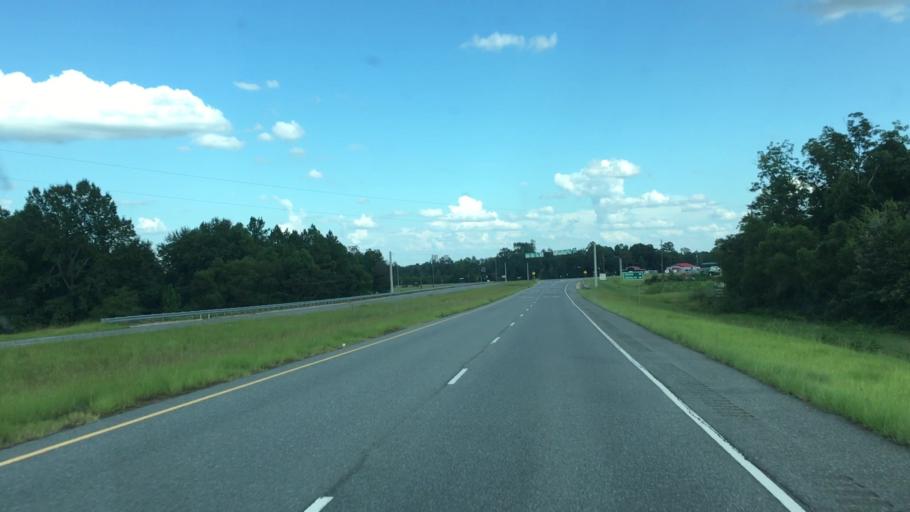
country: US
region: Georgia
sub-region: Laurens County
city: Dublin
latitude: 32.5006
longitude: -82.9328
